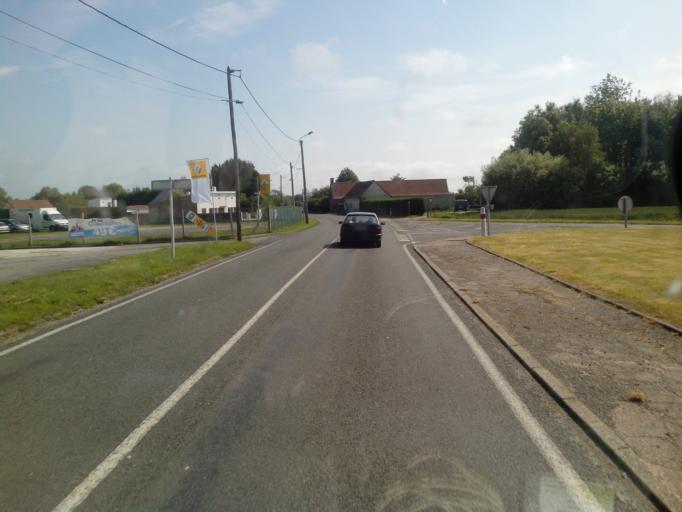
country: FR
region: Picardie
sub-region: Departement de la Somme
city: Quend
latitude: 50.3133
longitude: 1.6382
